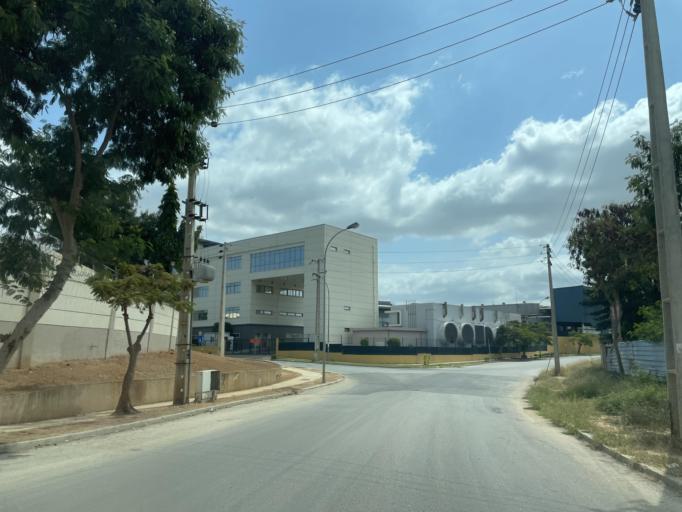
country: AO
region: Luanda
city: Luanda
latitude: -8.9304
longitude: 13.1865
